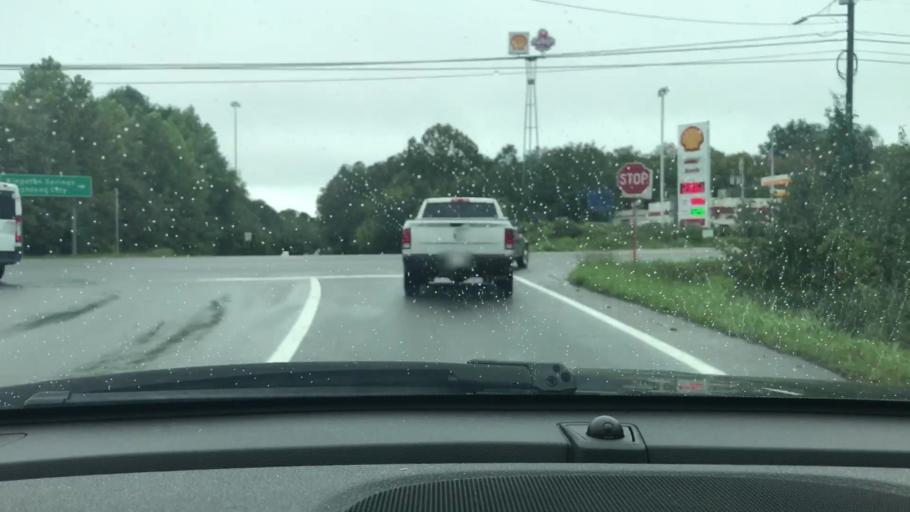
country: US
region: Tennessee
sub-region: Cheatham County
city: Kingston Springs
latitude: 36.0844
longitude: -87.0986
